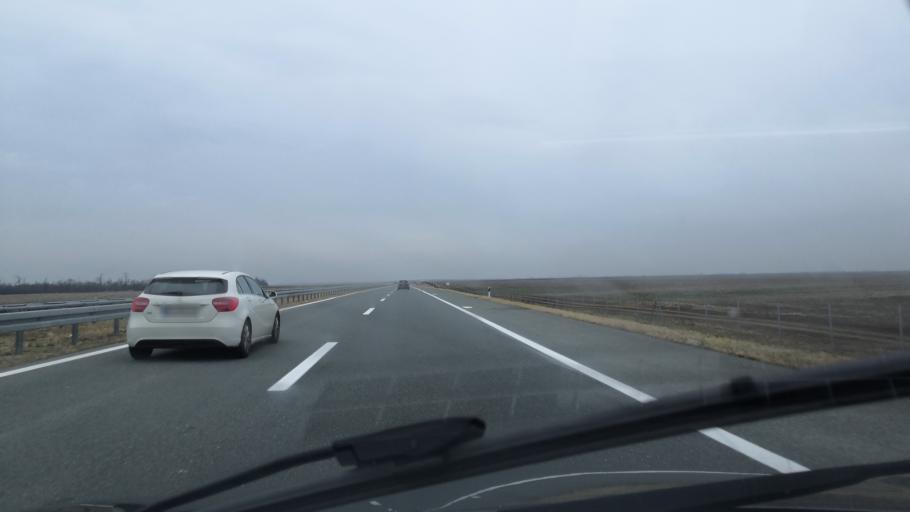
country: RS
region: Autonomna Pokrajina Vojvodina
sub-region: Severnobacki Okrug
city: Mali Igos
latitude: 45.7011
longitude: 19.7202
